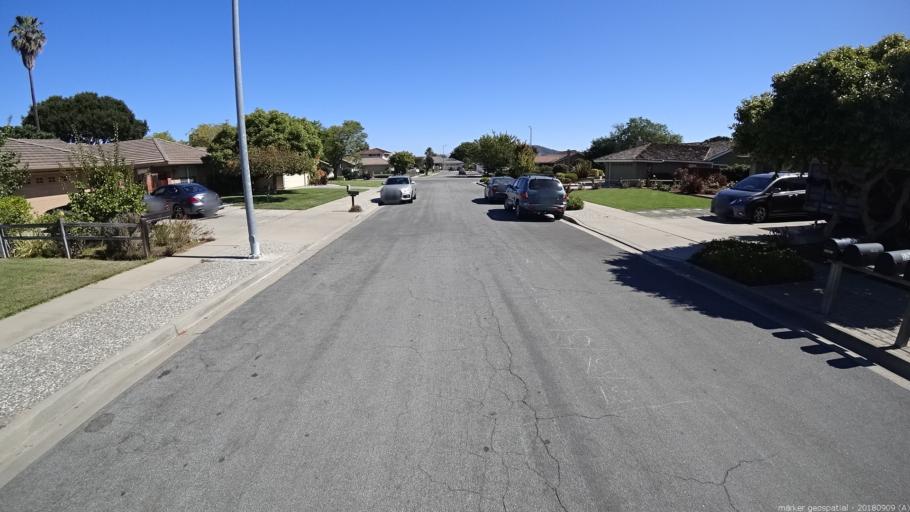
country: US
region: California
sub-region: Monterey County
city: Salinas
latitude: 36.5929
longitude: -121.7092
